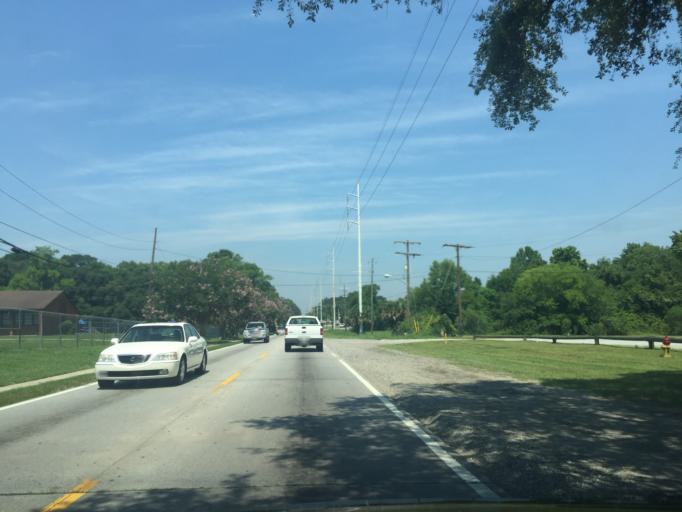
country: US
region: Georgia
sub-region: Chatham County
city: Savannah
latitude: 32.0493
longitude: -81.1180
